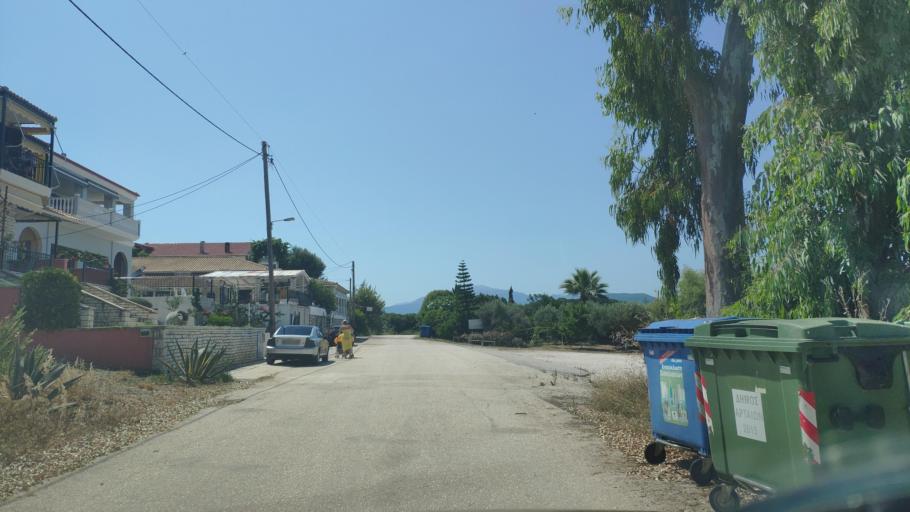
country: GR
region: Epirus
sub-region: Nomos Artas
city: Aneza
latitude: 39.0125
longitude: 20.9187
